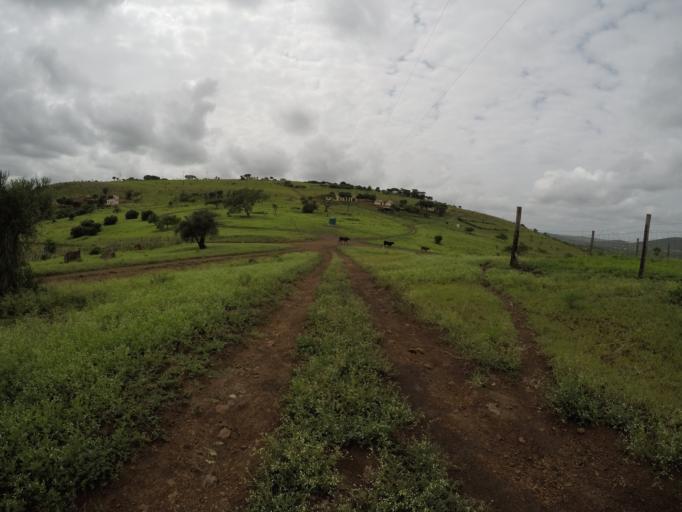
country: ZA
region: KwaZulu-Natal
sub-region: uThungulu District Municipality
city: Empangeni
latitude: -28.6173
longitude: 31.8920
